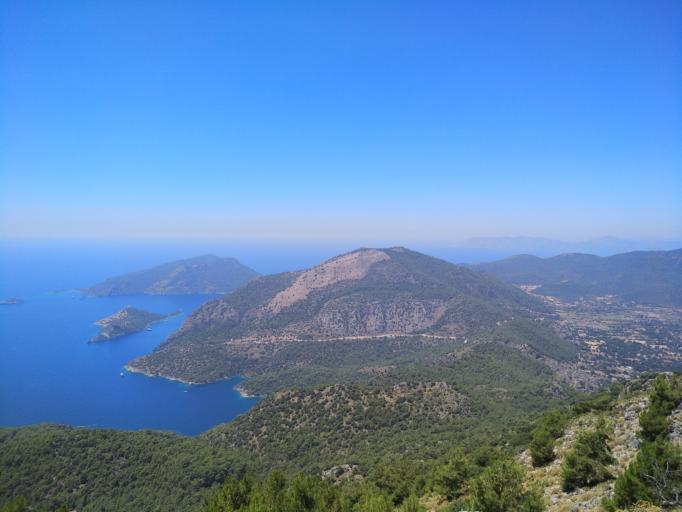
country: TR
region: Mugla
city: OEluedeniz
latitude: 36.5691
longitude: 29.1063
